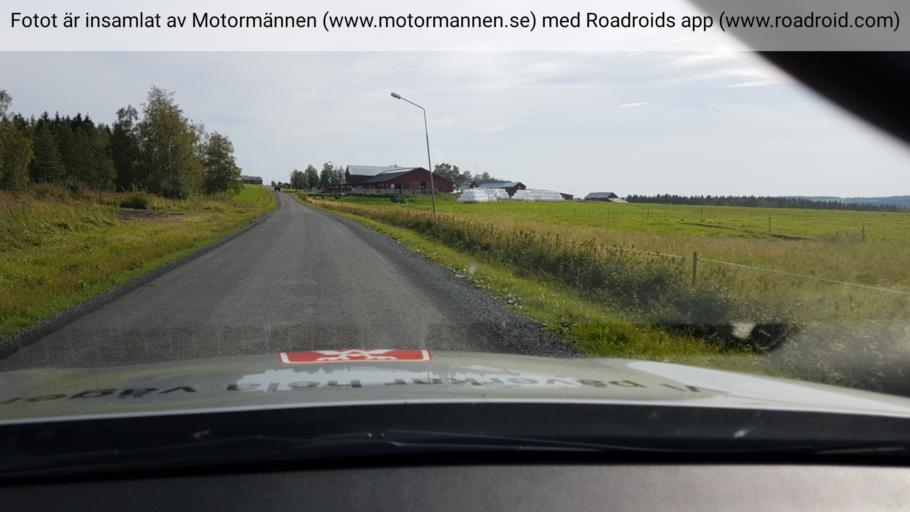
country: SE
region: Jaemtland
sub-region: Krokoms Kommun
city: Valla
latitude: 63.3579
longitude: 13.9716
